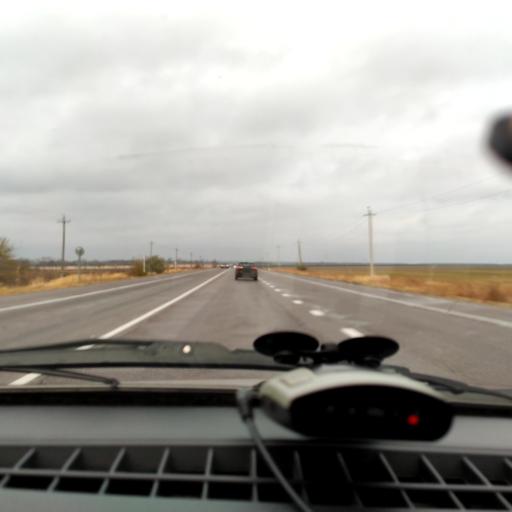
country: RU
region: Voronezj
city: Strelitsa
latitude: 51.5455
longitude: 38.9713
